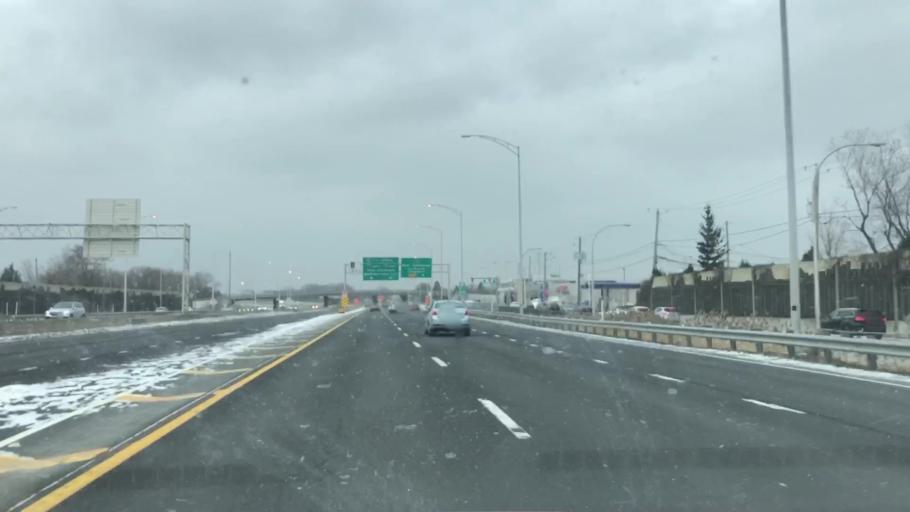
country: CA
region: Quebec
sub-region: Monteregie
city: Brossard
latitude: 45.4608
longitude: -73.4531
